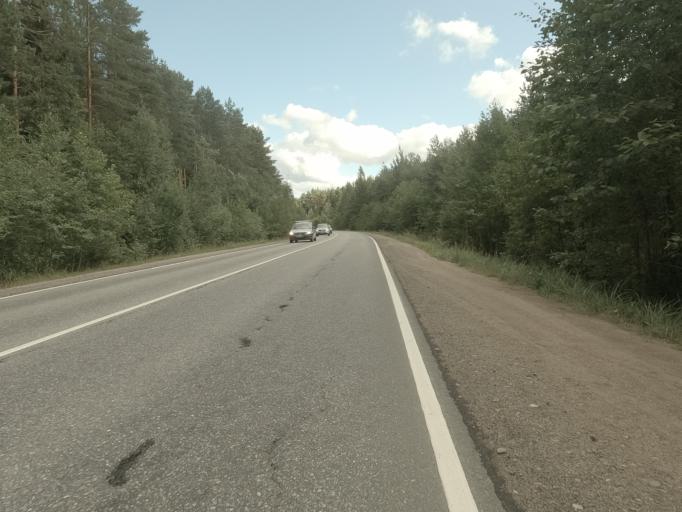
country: RU
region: Leningrad
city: Shcheglovo
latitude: 60.0110
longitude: 30.8558
